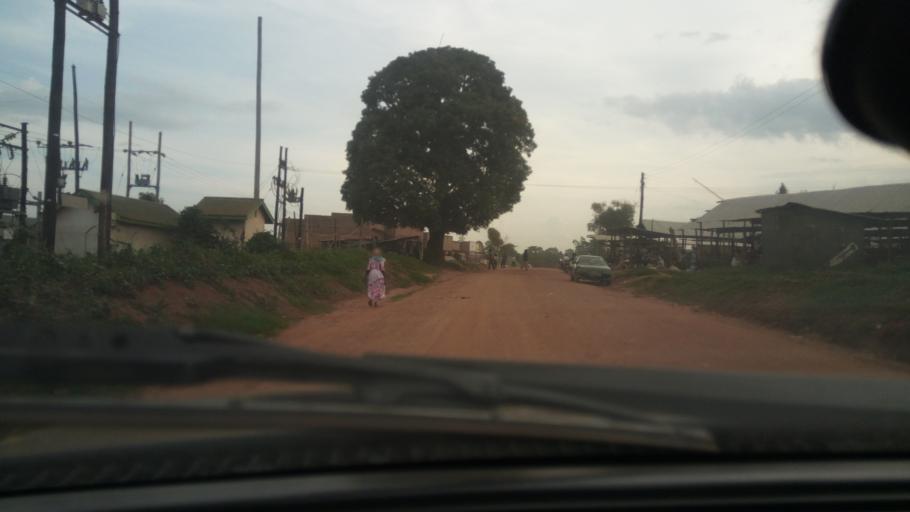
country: UG
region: Central Region
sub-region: Mityana District
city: Mityana
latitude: 0.5645
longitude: 32.2055
